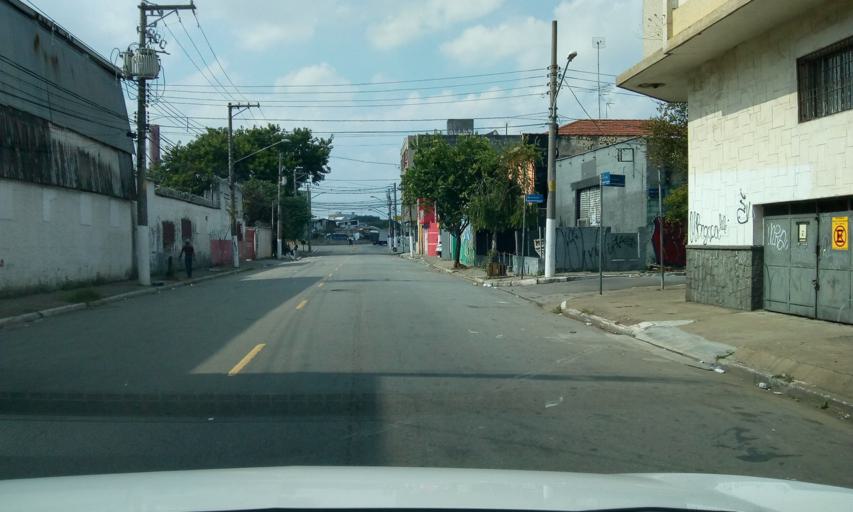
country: BR
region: Sao Paulo
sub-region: Sao Paulo
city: Sao Paulo
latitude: -23.5223
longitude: -46.6402
